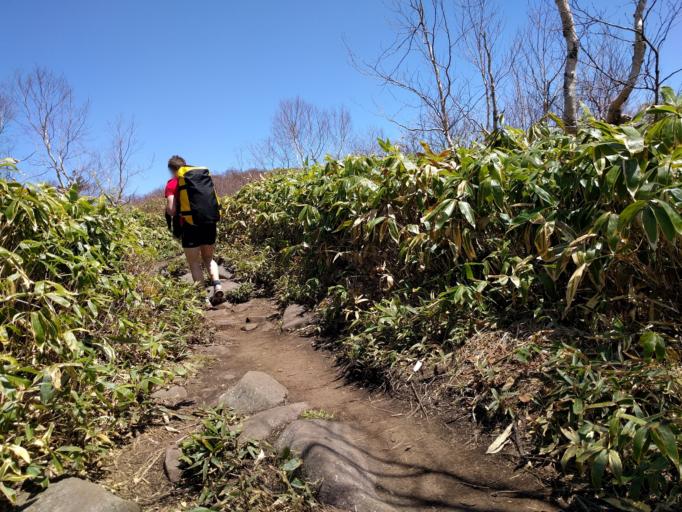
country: JP
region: Nagano
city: Nagano-shi
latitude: 36.7378
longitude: 138.1320
